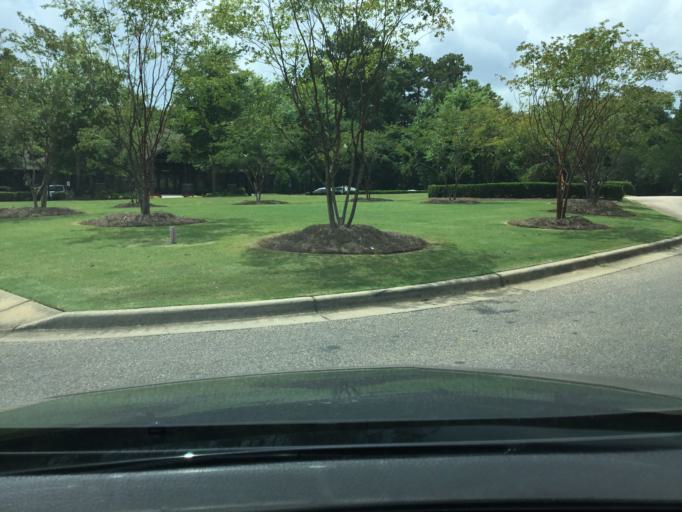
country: US
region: Alabama
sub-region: Montgomery County
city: Pike Road
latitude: 32.3445
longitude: -86.0819
